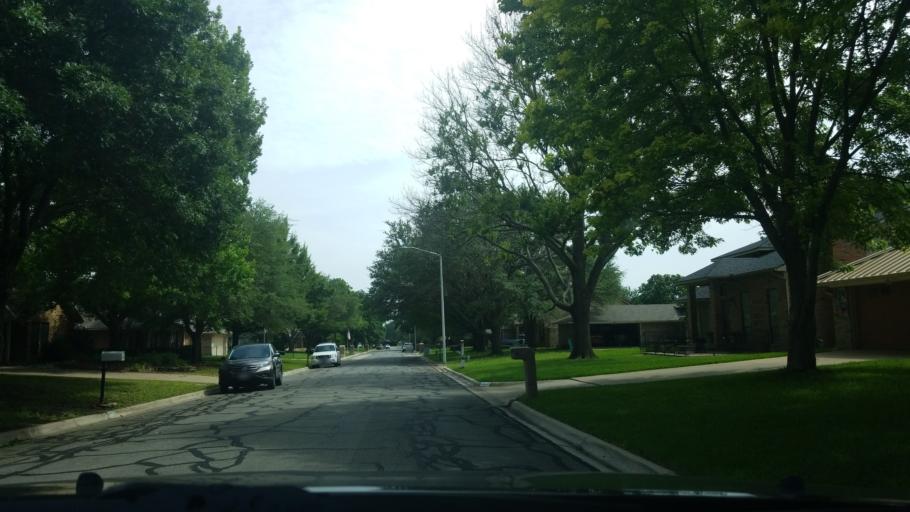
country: US
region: Texas
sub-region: Denton County
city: Denton
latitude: 33.2350
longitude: -97.1525
